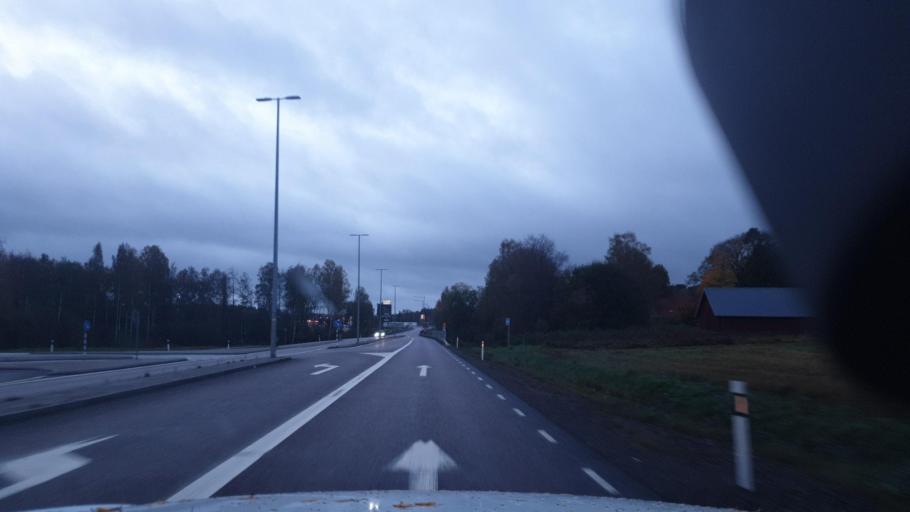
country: SE
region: Vaermland
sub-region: Eda Kommun
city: Charlottenberg
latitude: 59.8841
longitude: 12.2829
